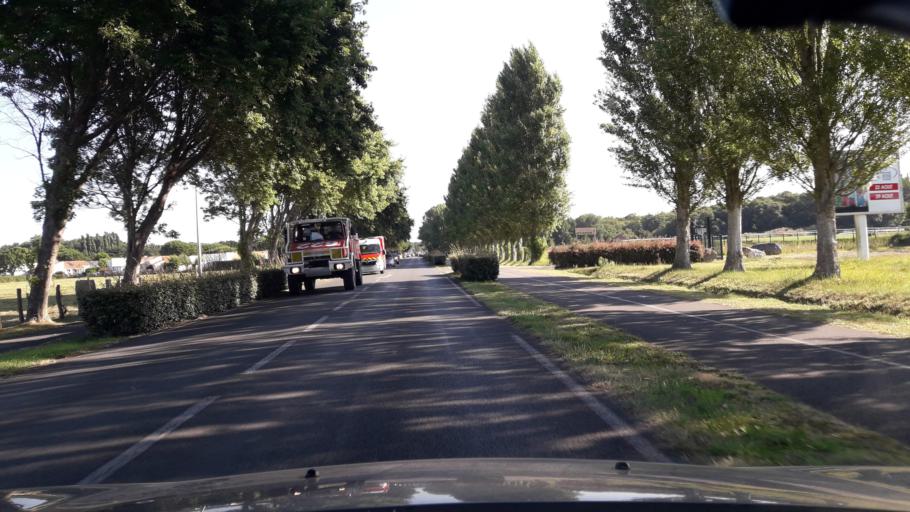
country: FR
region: Poitou-Charentes
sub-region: Departement de la Charente-Maritime
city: Les Mathes
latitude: 45.6971
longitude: -1.1743
